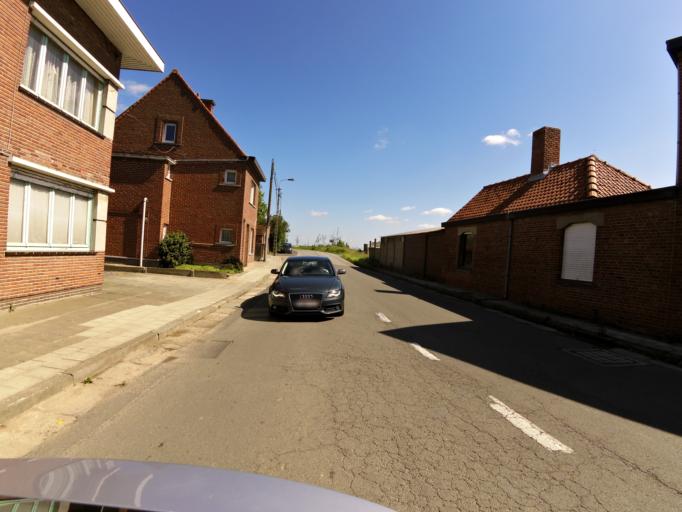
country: BE
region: Flanders
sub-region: Provincie West-Vlaanderen
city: Ieper
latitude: 50.8866
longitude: 2.8180
